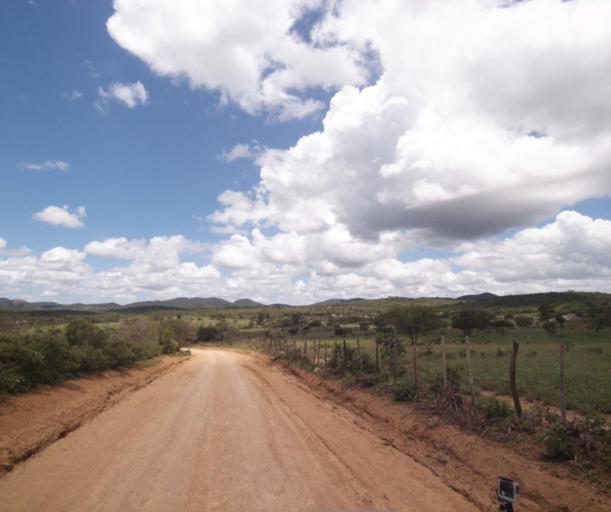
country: BR
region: Bahia
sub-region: Pocoes
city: Pocoes
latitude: -14.3806
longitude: -40.3753
